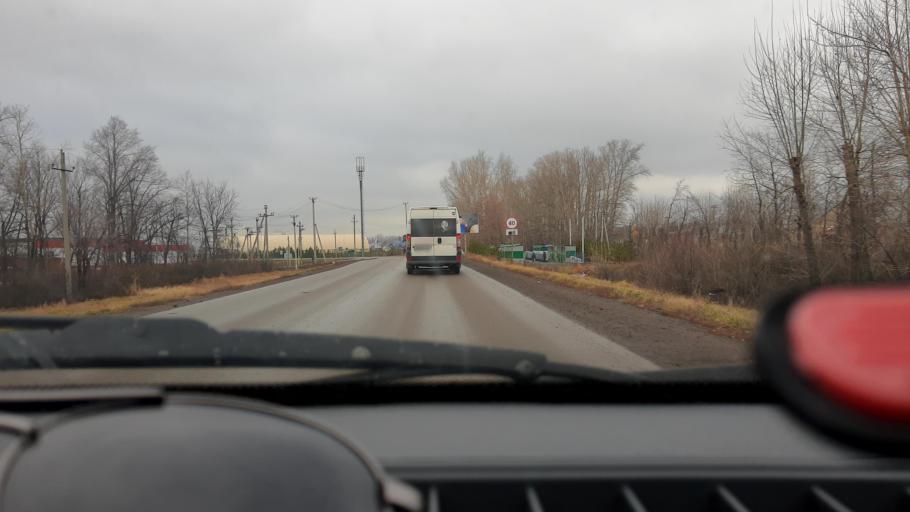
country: RU
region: Bashkortostan
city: Ufa
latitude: 54.6293
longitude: 55.9191
